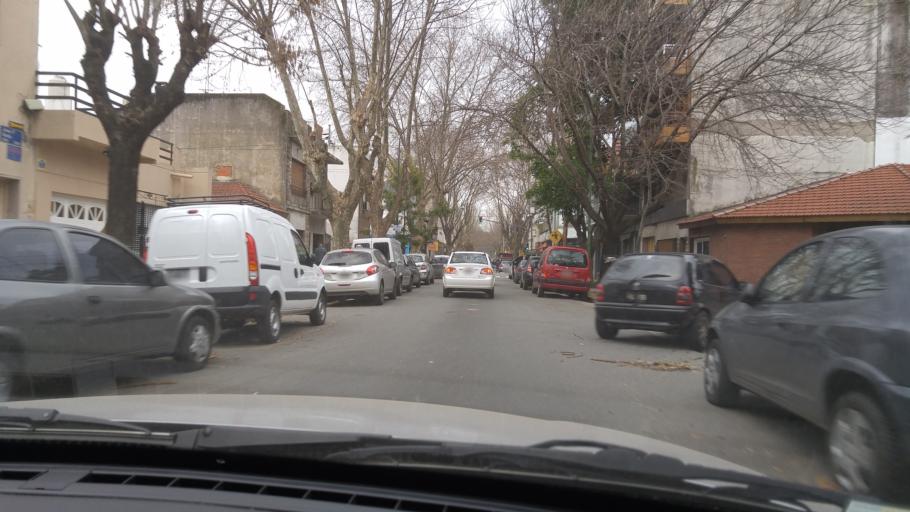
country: AR
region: Buenos Aires F.D.
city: Villa Santa Rita
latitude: -34.6160
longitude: -58.5236
